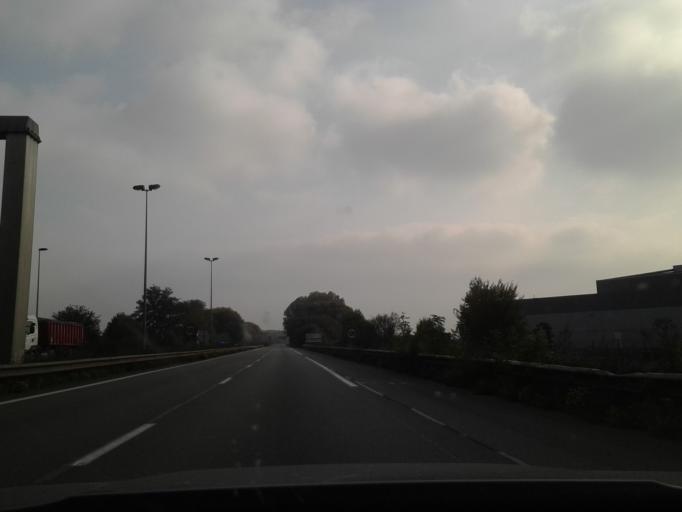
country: FR
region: Nord-Pas-de-Calais
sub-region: Departement du Nord
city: Sainghin-en-Melantois
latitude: 50.5983
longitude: 3.1473
